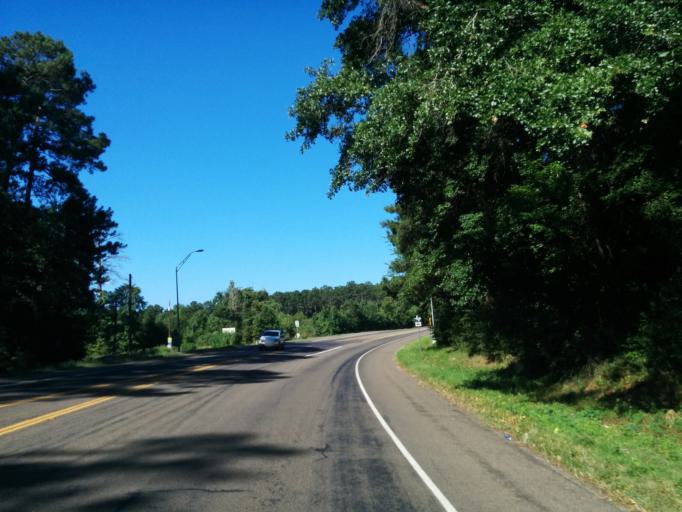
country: US
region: Texas
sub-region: Sabine County
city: Milam
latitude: 31.4360
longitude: -93.7824
